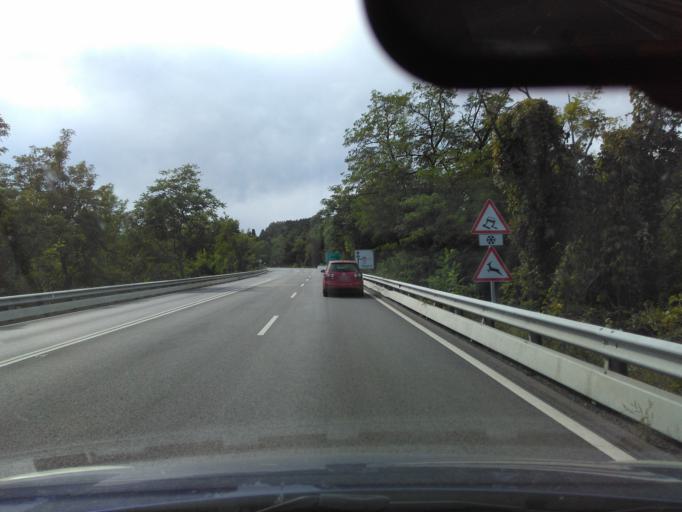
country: HU
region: Pest
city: Kerepes
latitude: 47.5881
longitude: 19.3022
